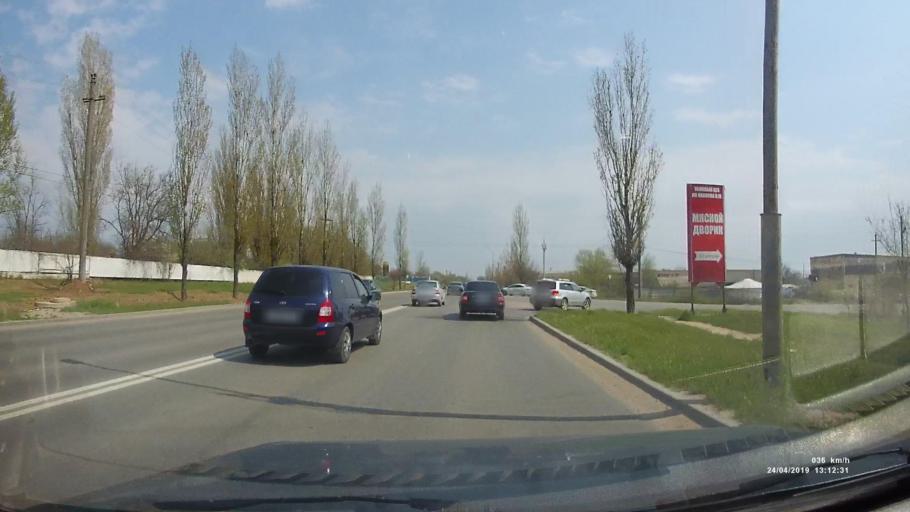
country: RU
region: Kalmykiya
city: Elista
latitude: 46.3126
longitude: 44.3040
